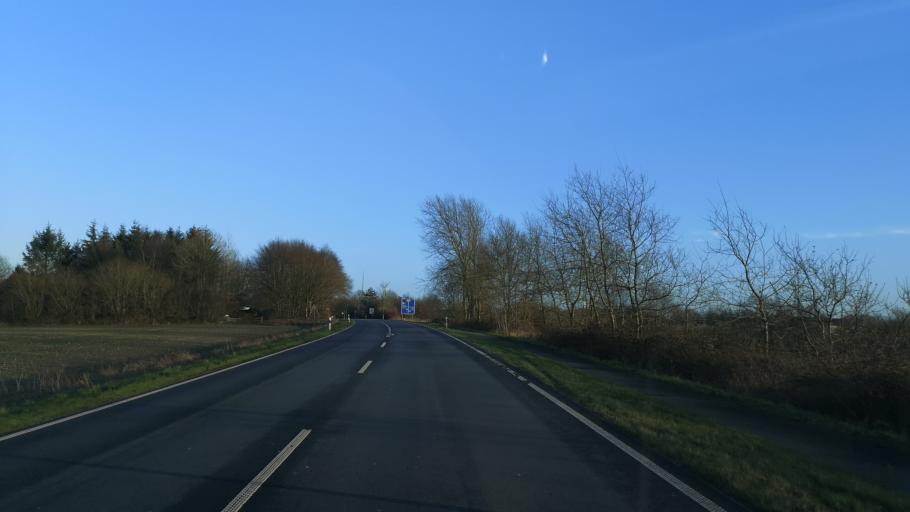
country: DE
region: Schleswig-Holstein
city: Tarp
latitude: 54.6642
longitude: 9.4207
